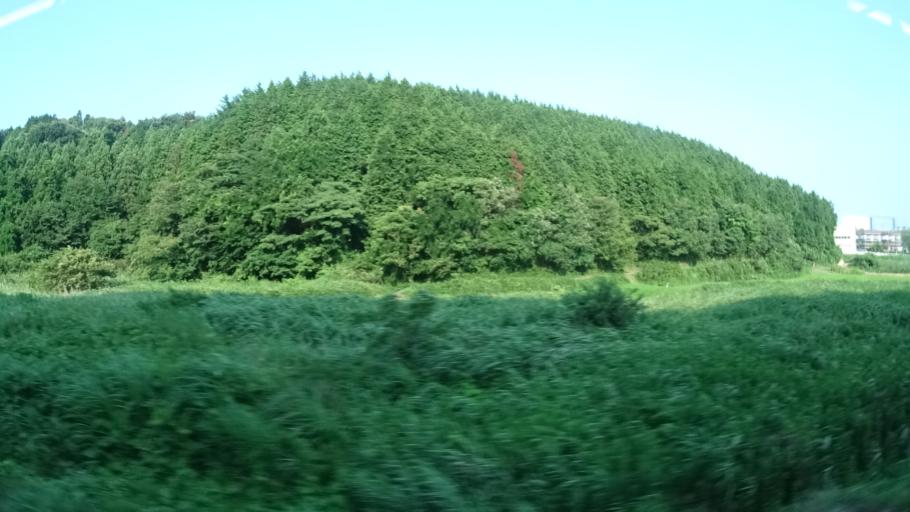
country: JP
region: Ibaraki
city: Takahagi
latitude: 36.7350
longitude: 140.7194
